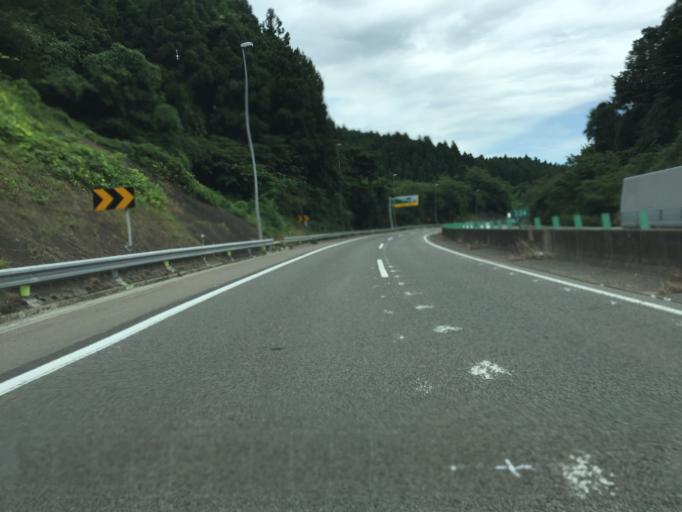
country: JP
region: Miyagi
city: Sendai
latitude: 38.1999
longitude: 140.7860
